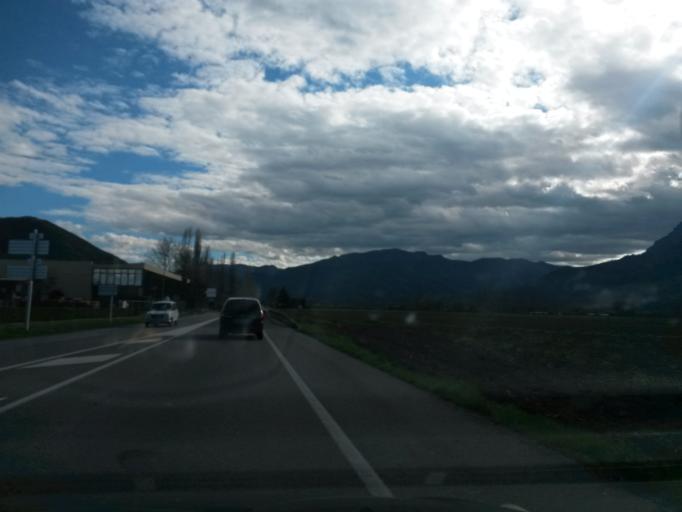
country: ES
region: Catalonia
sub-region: Provincia de Girona
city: Olot
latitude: 42.1552
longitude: 2.4647
